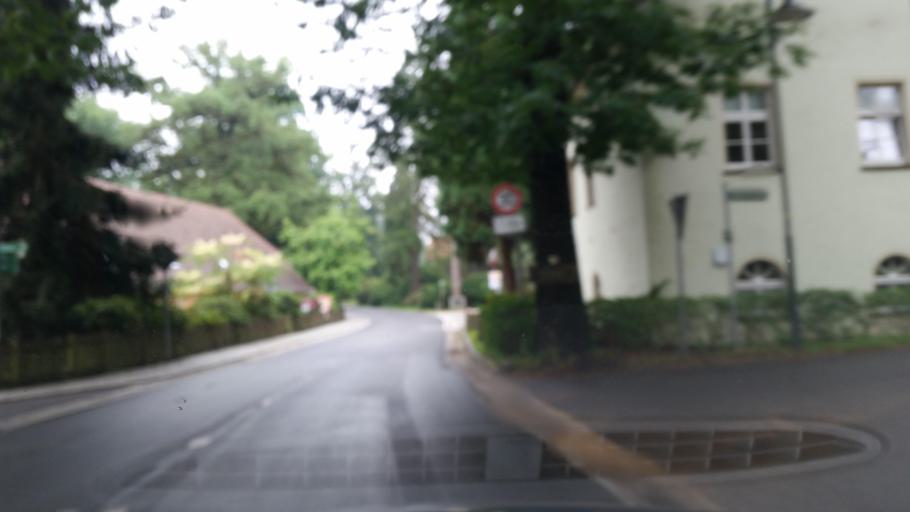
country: DE
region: Saxony
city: Weisswasser
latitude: 51.5373
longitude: 14.6309
